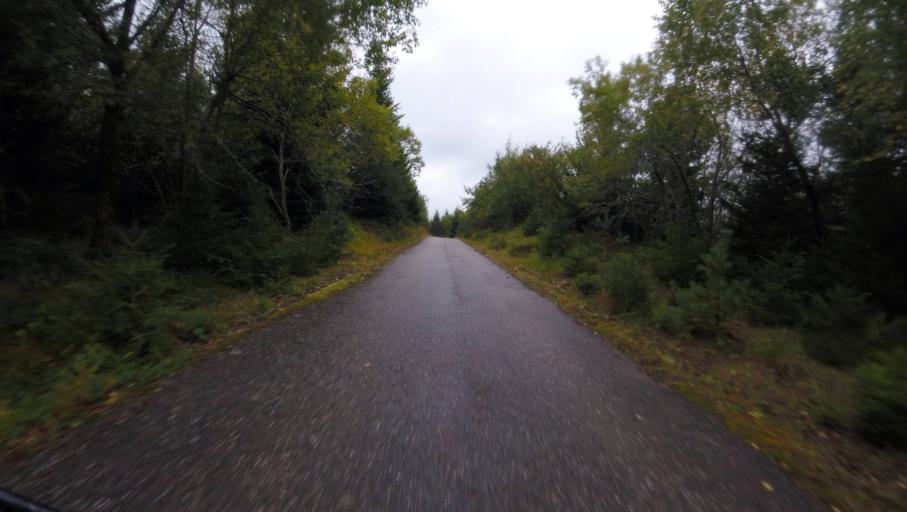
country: DE
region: Baden-Wuerttemberg
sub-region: Karlsruhe Region
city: Weisenbach
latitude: 48.7104
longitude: 8.4153
